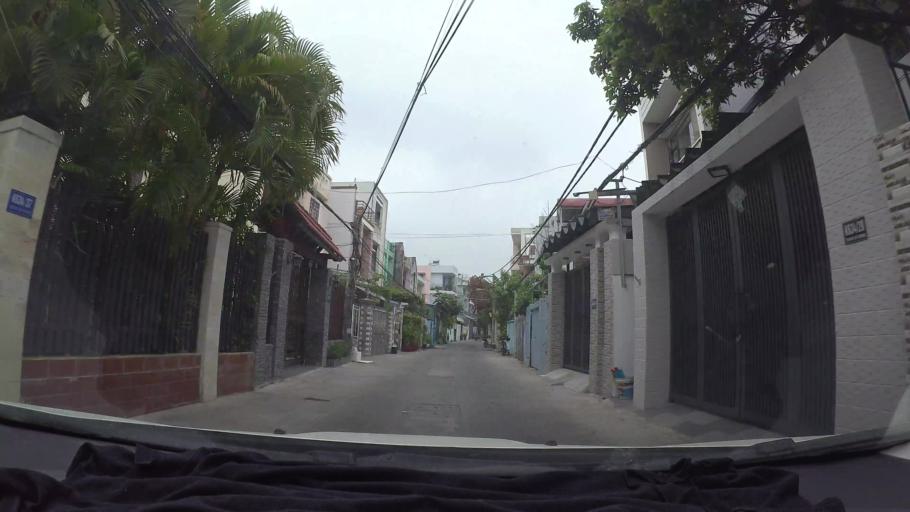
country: VN
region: Da Nang
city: Da Nang
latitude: 16.0450
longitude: 108.2073
